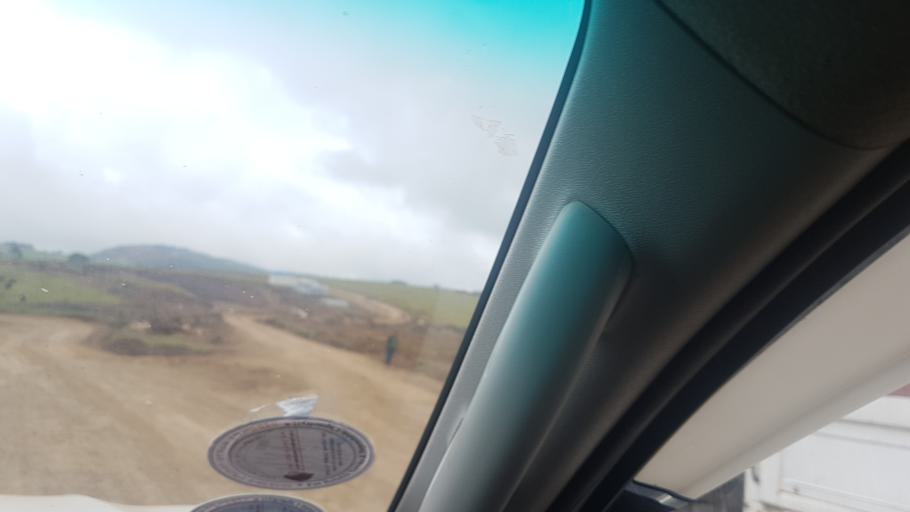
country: ET
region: Southern Nations, Nationalities, and People's Region
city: Arba Minch'
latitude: 6.3265
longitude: 37.5471
